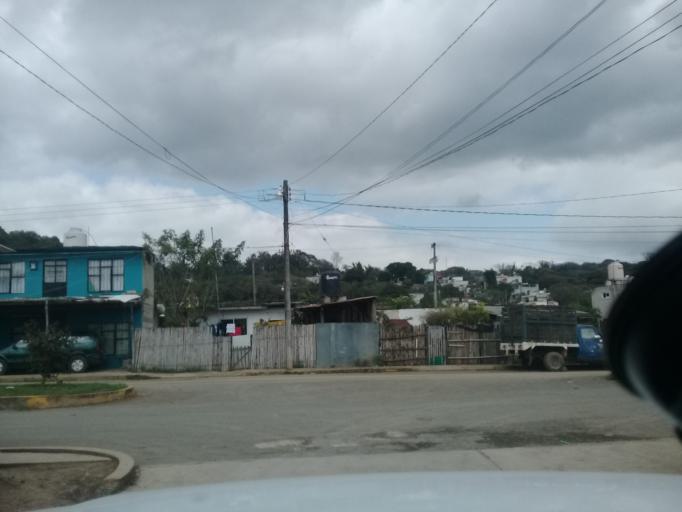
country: MX
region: Veracruz
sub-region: Xalapa
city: Fraccionamiento las Fuentes
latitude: 19.4739
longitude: -96.8785
